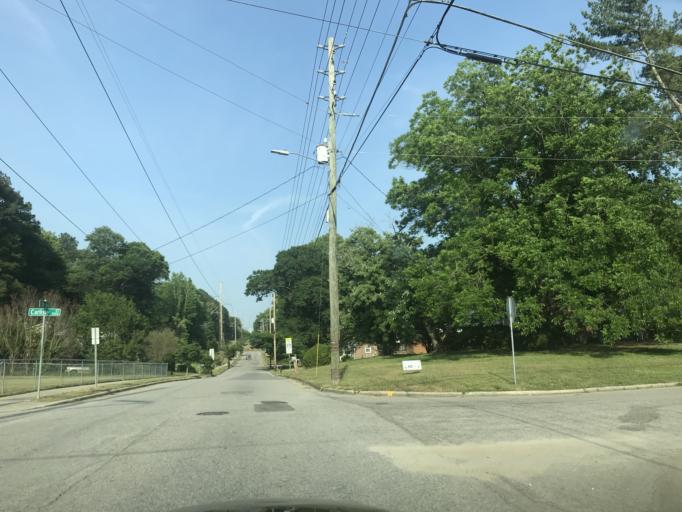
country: US
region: North Carolina
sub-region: Wake County
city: Raleigh
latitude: 35.7634
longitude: -78.5911
